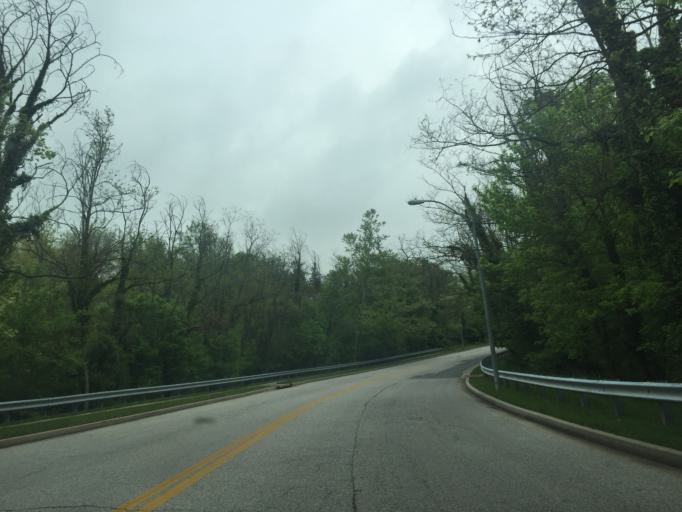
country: US
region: Maryland
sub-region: Baltimore County
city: Catonsville
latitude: 39.2503
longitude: -76.7288
